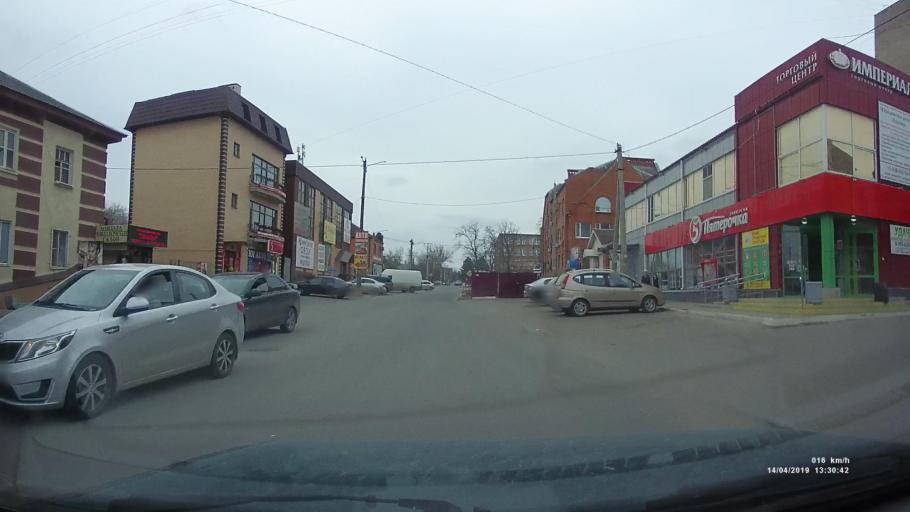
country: RU
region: Rostov
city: Azov
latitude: 47.1059
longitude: 39.4308
